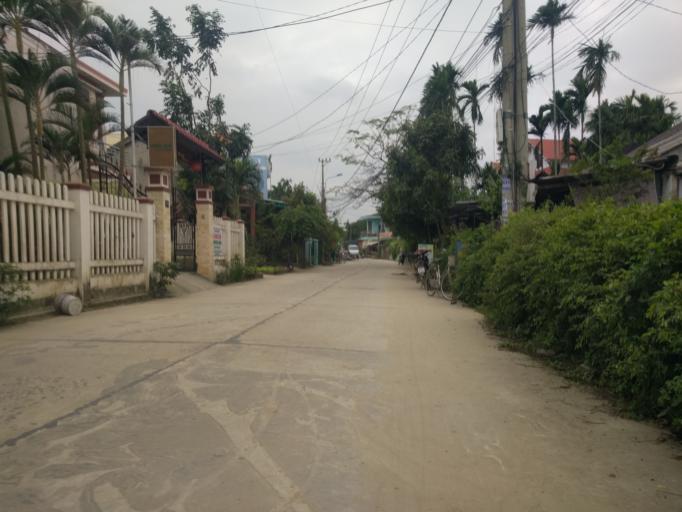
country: VN
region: Quang Nam
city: Hoi An
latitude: 15.8697
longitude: 108.3497
